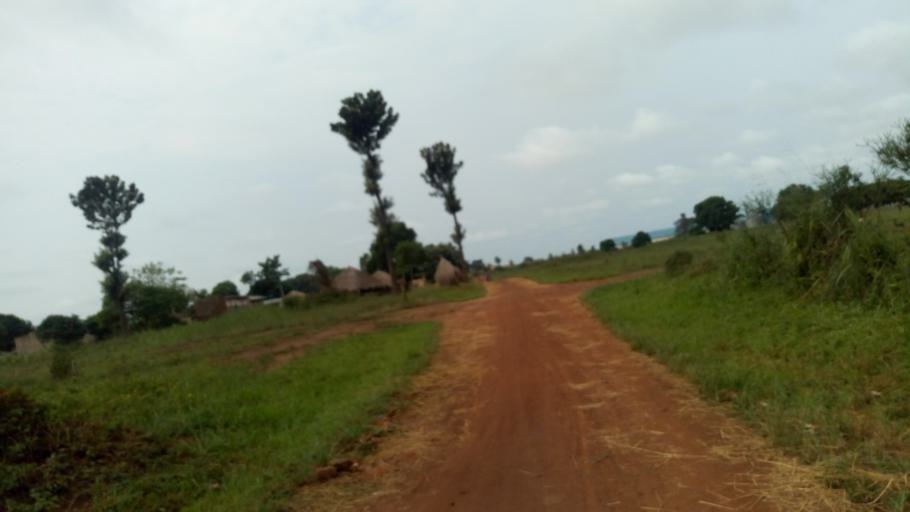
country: UG
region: Western Region
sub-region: Kiryandongo District
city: Kiryandongo
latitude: 1.8013
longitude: 32.0128
